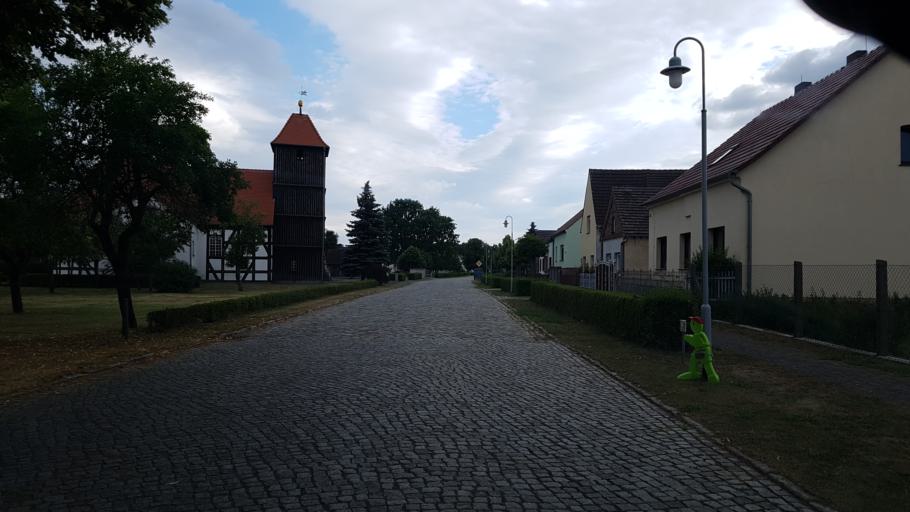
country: DE
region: Brandenburg
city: Kasel-Golzig
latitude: 51.9867
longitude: 13.6948
